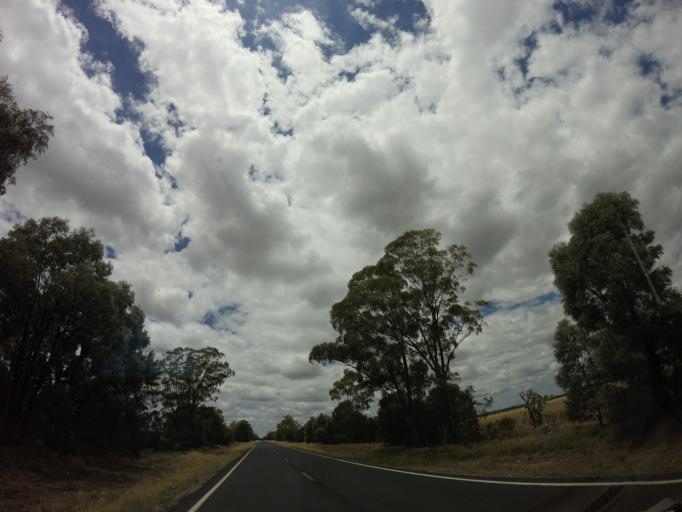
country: AU
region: Queensland
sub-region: Goondiwindi
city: Goondiwindi
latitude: -28.1699
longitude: 150.5103
